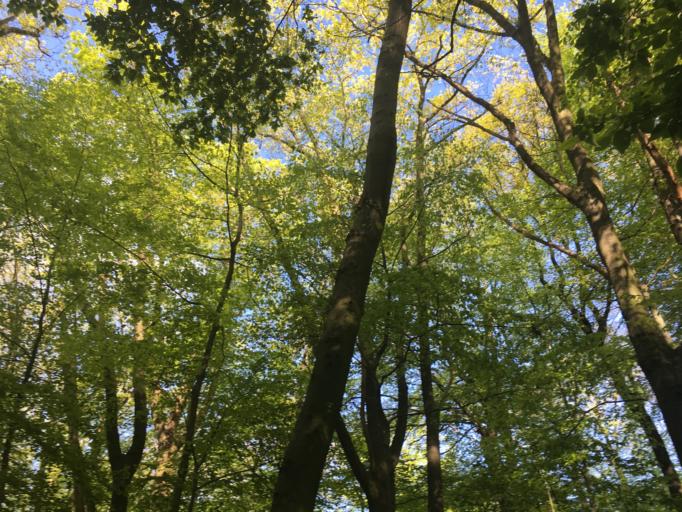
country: DE
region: North Rhine-Westphalia
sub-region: Regierungsbezirk Dusseldorf
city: Ratingen
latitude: 51.2414
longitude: 6.8355
